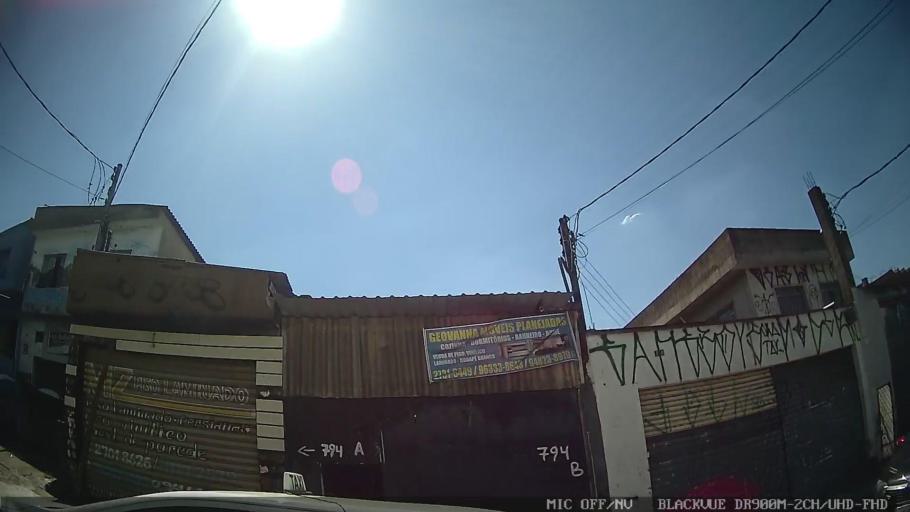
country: BR
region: Sao Paulo
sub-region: Sao Caetano Do Sul
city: Sao Caetano do Sul
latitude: -23.5978
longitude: -46.5104
